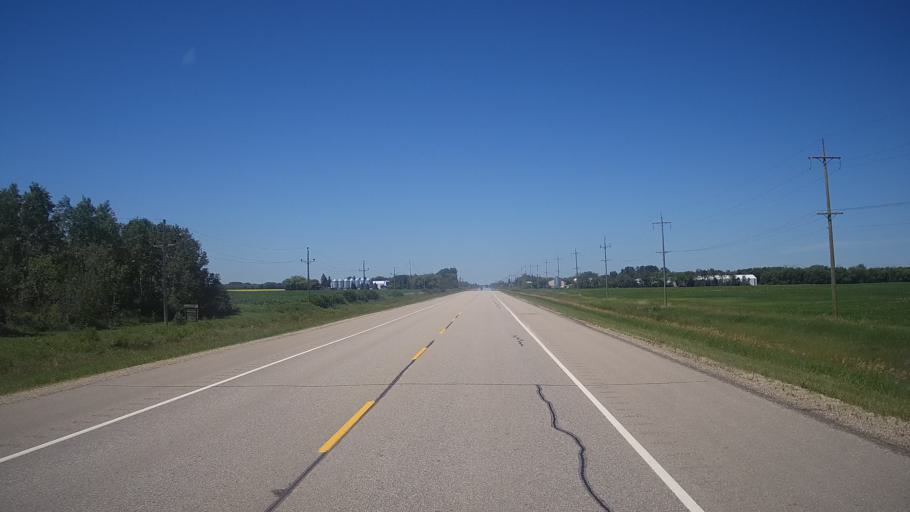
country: CA
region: Manitoba
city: Neepawa
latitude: 50.2252
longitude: -99.3088
